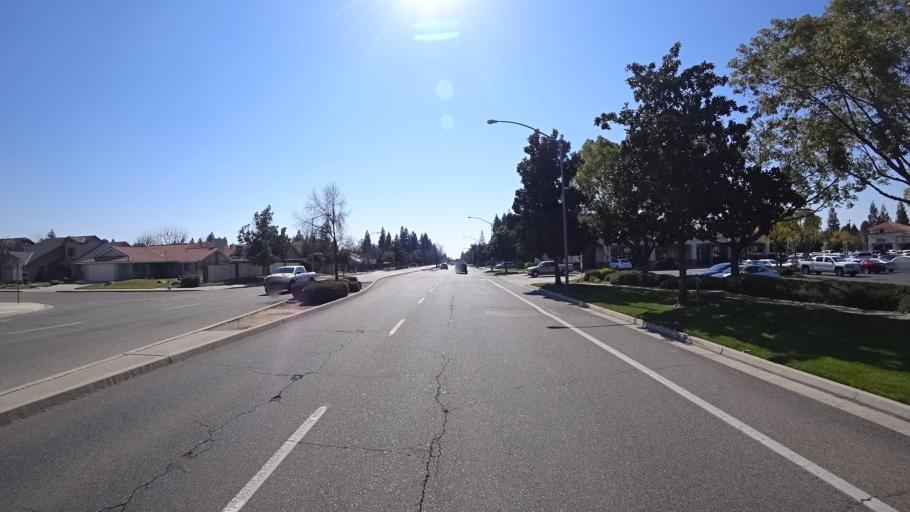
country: US
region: California
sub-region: Fresno County
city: Clovis
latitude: 36.8648
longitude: -119.7569
